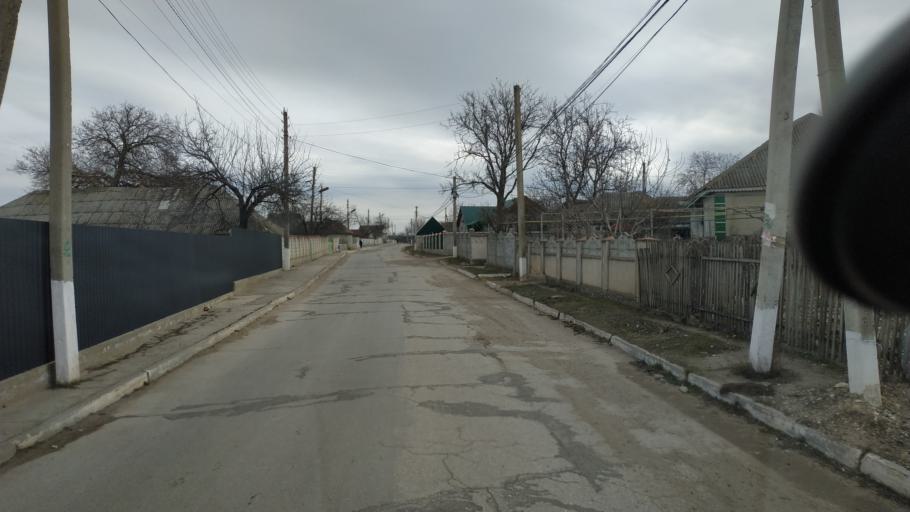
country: MD
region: Telenesti
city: Cocieri
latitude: 47.3835
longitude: 29.1156
